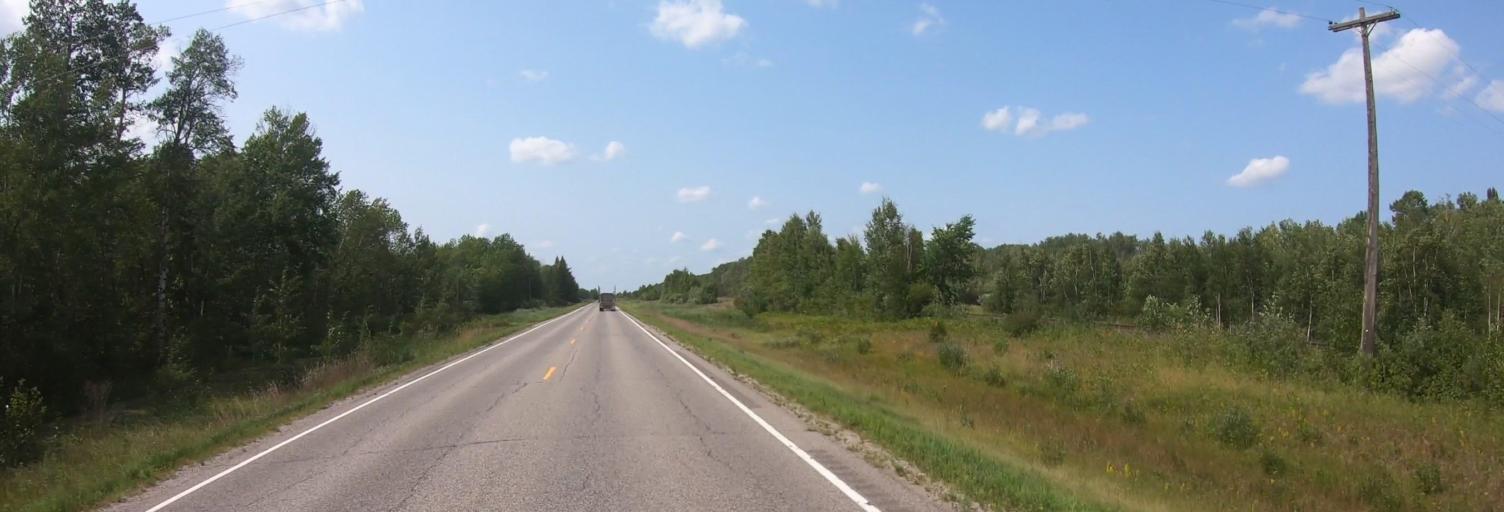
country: US
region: Minnesota
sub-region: Roseau County
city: Warroad
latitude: 48.8132
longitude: -95.1240
